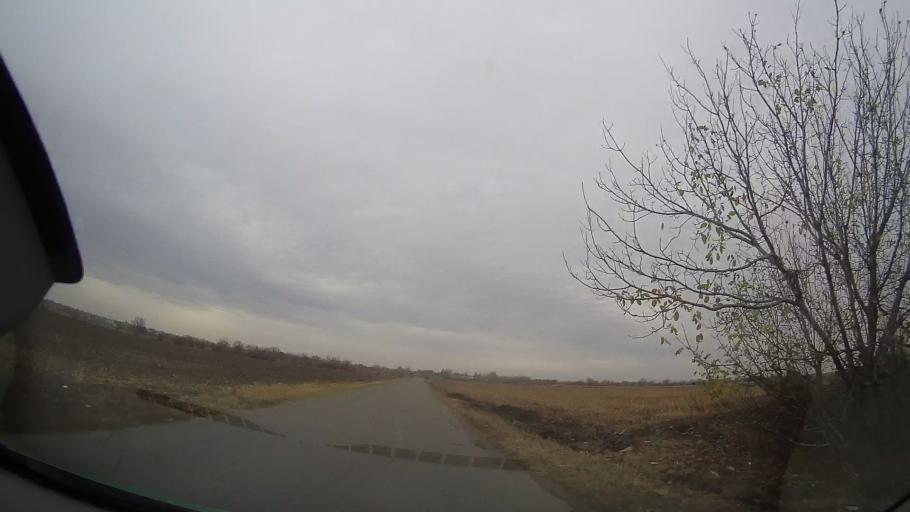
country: RO
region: Prahova
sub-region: Comuna Fantanele
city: Fantanele
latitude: 45.0081
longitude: 26.3585
